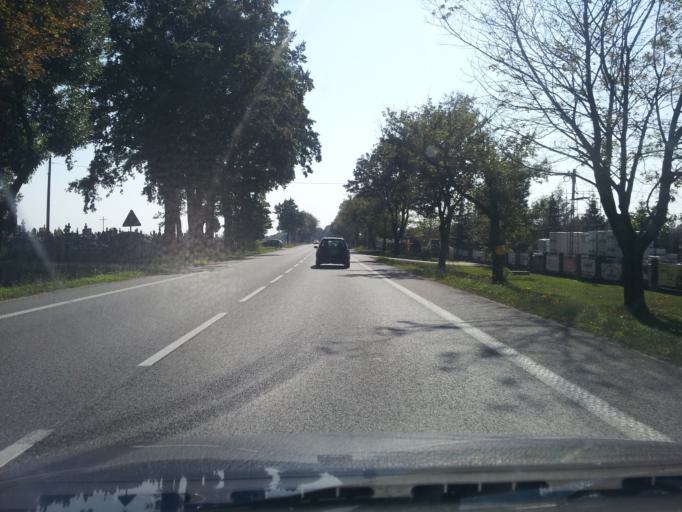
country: PL
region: Masovian Voivodeship
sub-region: Powiat sierpecki
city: Sierpc
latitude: 52.8483
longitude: 19.7093
